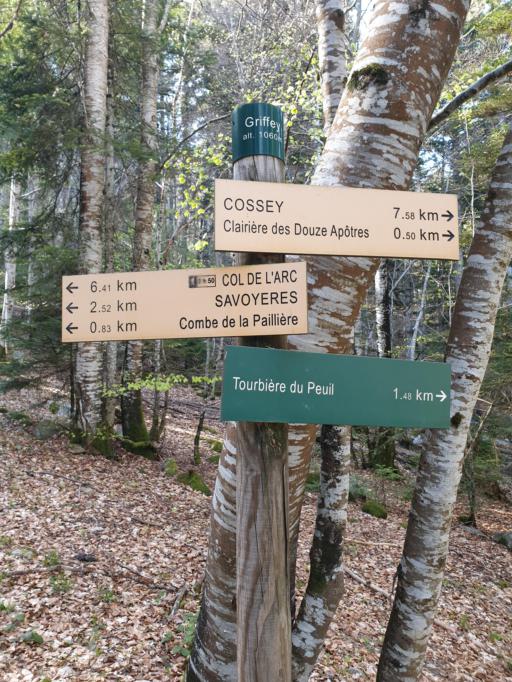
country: FR
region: Rhone-Alpes
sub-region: Departement de l'Isere
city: Claix
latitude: 45.1130
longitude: 5.6414
